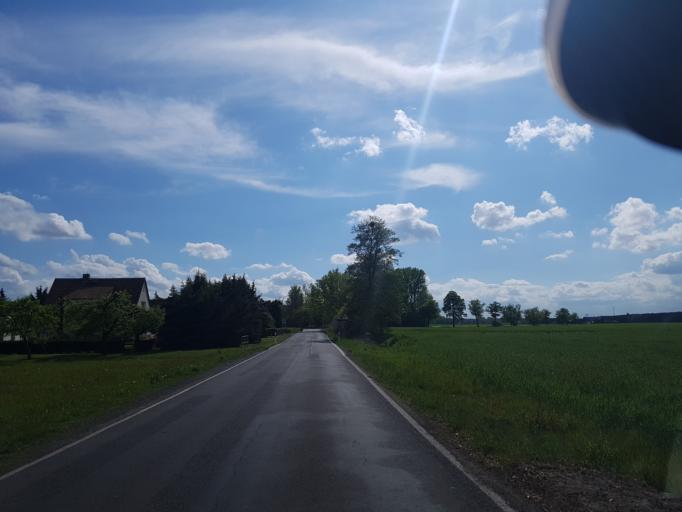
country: DE
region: Brandenburg
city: Heinersbruck
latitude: 51.6832
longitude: 14.4696
